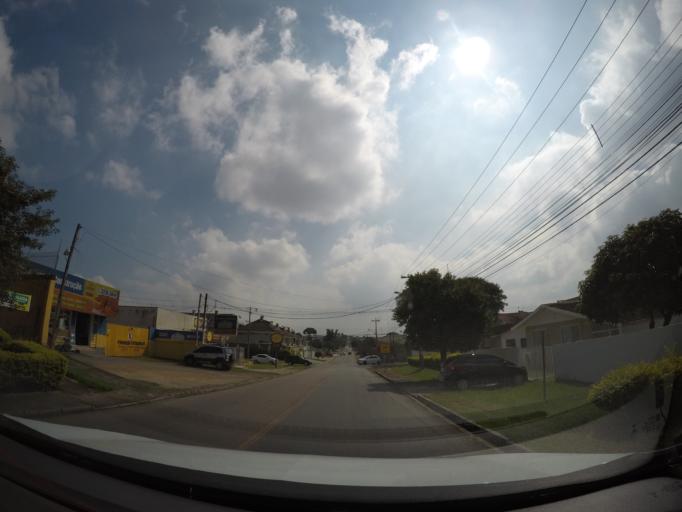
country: BR
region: Parana
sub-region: Sao Jose Dos Pinhais
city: Sao Jose dos Pinhais
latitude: -25.4949
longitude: -49.2533
